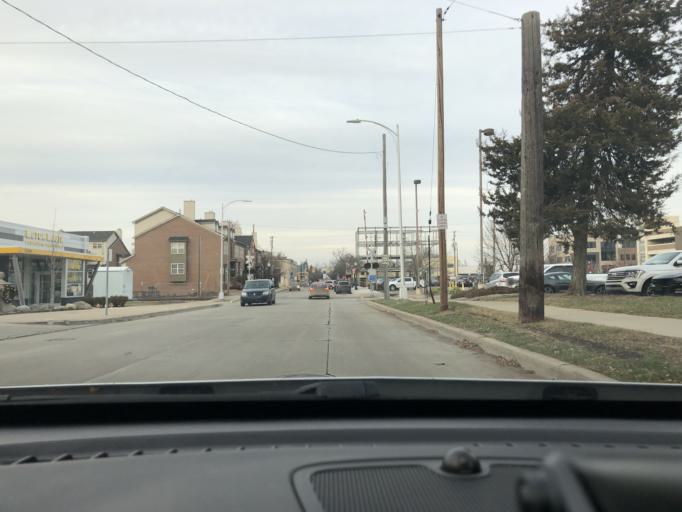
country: US
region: Michigan
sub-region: Wayne County
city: Dearborn Heights
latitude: 42.3039
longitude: -83.2452
